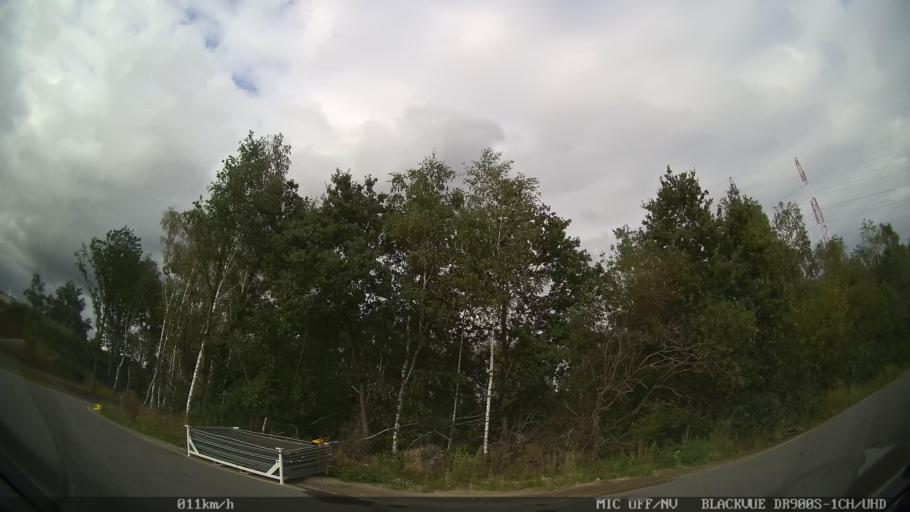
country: BE
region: Flanders
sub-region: Provincie Limburg
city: Zutendaal
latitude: 50.9140
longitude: 5.5408
